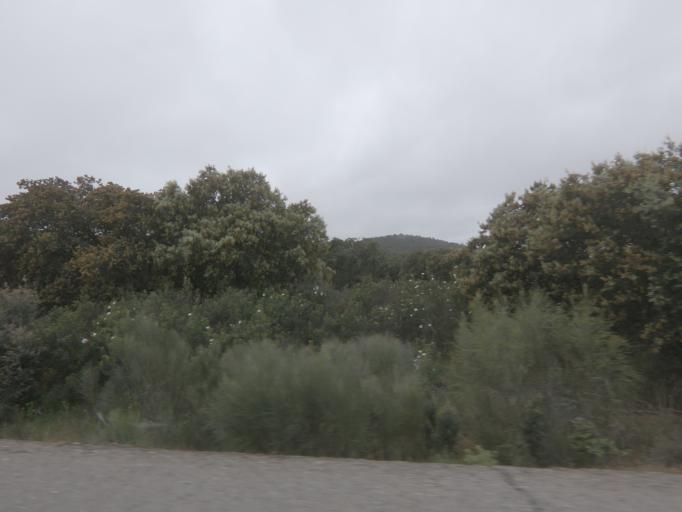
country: ES
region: Extremadura
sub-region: Provincia de Badajoz
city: Puebla de Obando
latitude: 39.2831
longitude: -6.5218
